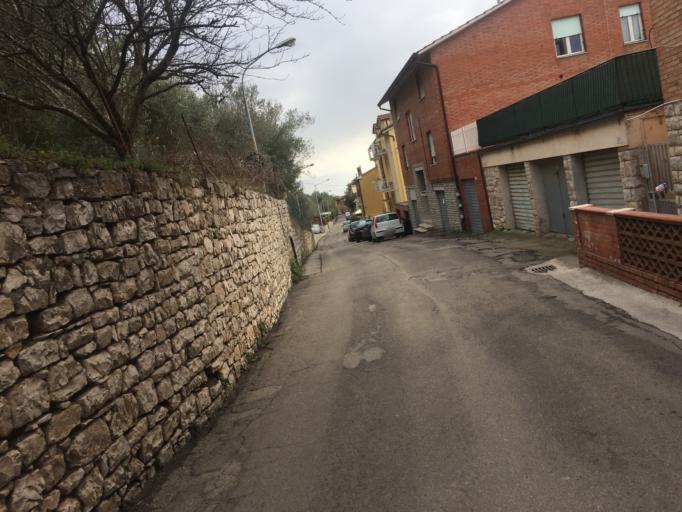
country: IT
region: Umbria
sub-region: Provincia di Perugia
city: Perugia
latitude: 43.1184
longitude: 12.4048
